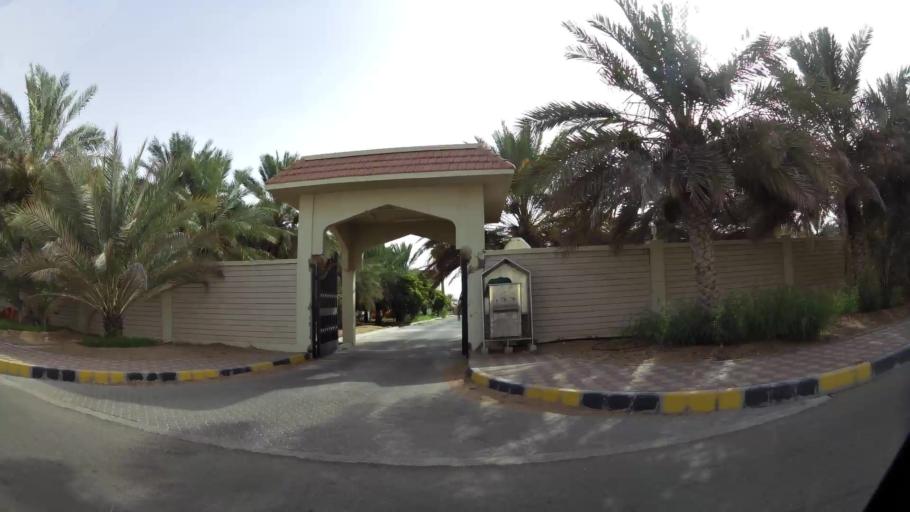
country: AE
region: Abu Dhabi
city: Al Ain
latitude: 24.1913
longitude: 55.6025
